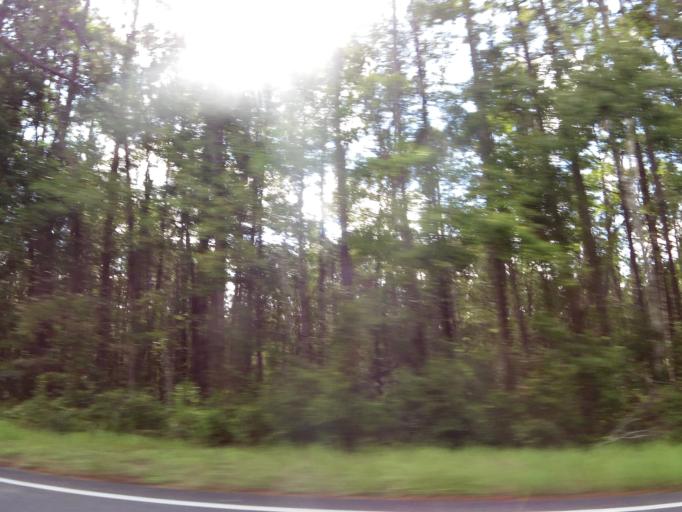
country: US
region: Georgia
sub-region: Camden County
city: Kingsland
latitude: 30.7517
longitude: -81.6876
